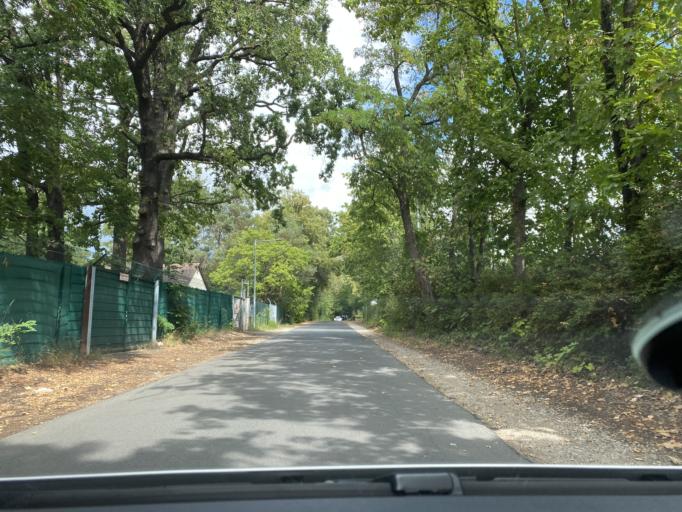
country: DE
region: Bavaria
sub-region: Regierungsbezirk Mittelfranken
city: Furth
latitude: 49.4963
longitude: 10.9952
